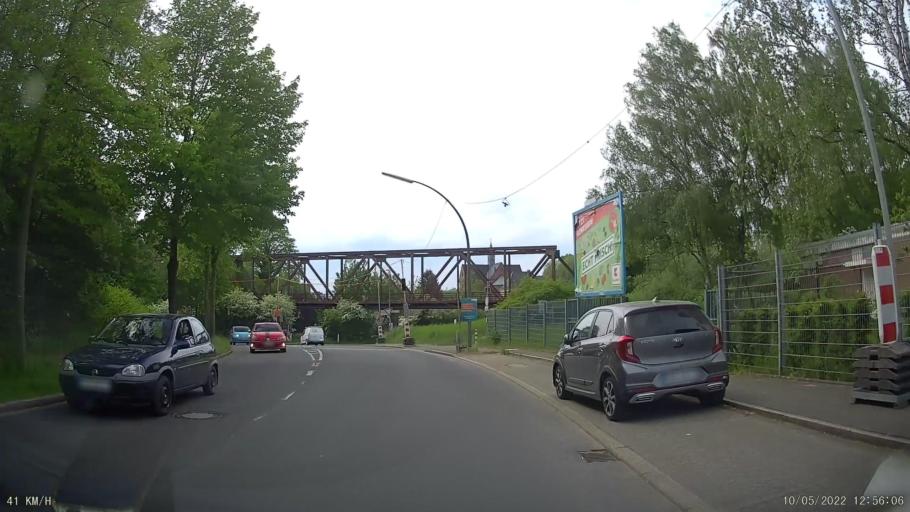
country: DE
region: North Rhine-Westphalia
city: Castrop-Rauxel
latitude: 51.5264
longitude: 7.3276
